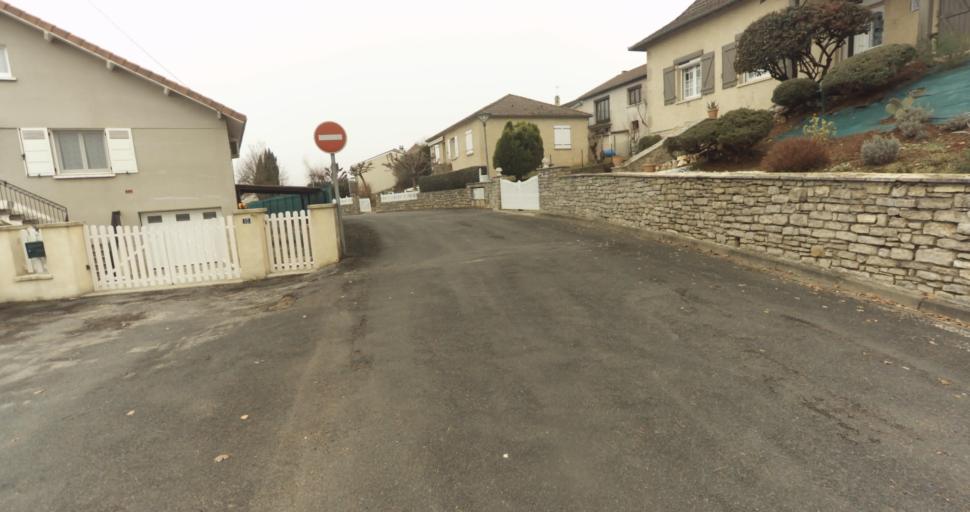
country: FR
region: Midi-Pyrenees
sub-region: Departement du Lot
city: Figeac
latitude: 44.6155
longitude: 2.0367
